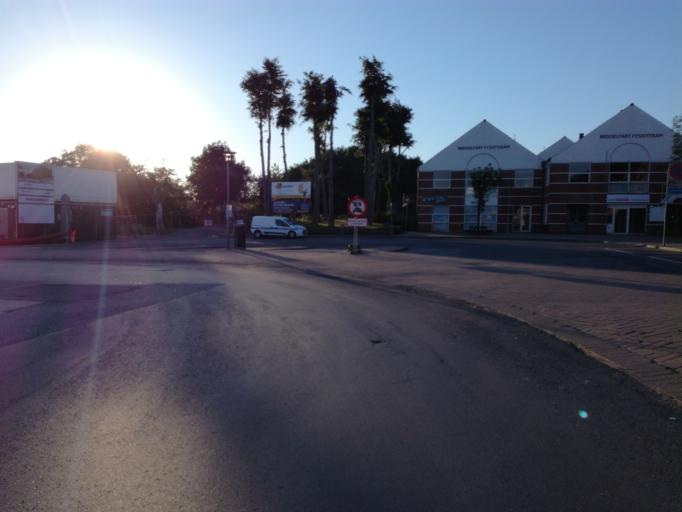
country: DK
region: South Denmark
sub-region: Middelfart Kommune
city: Middelfart
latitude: 55.5021
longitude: 9.7341
